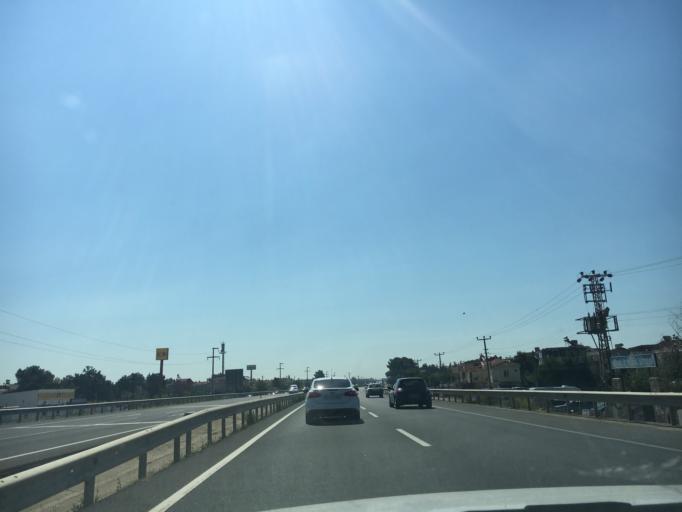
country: TR
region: Tekirdag
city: Marmara Ereglisi
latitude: 40.9931
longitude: 27.8437
